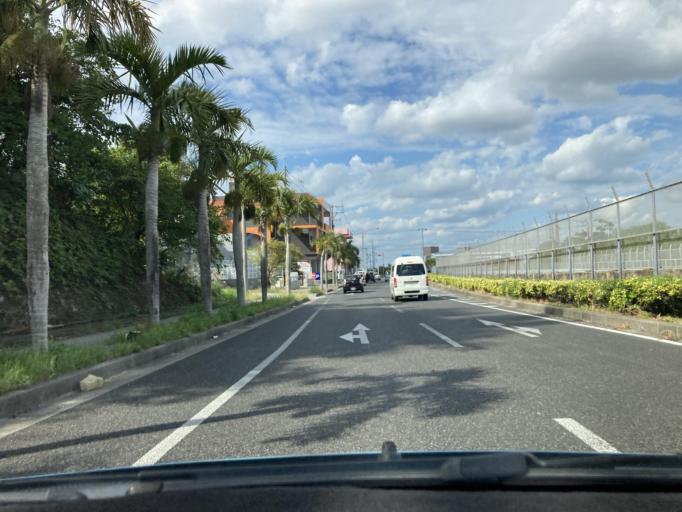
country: JP
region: Okinawa
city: Okinawa
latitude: 26.3291
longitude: 127.7848
